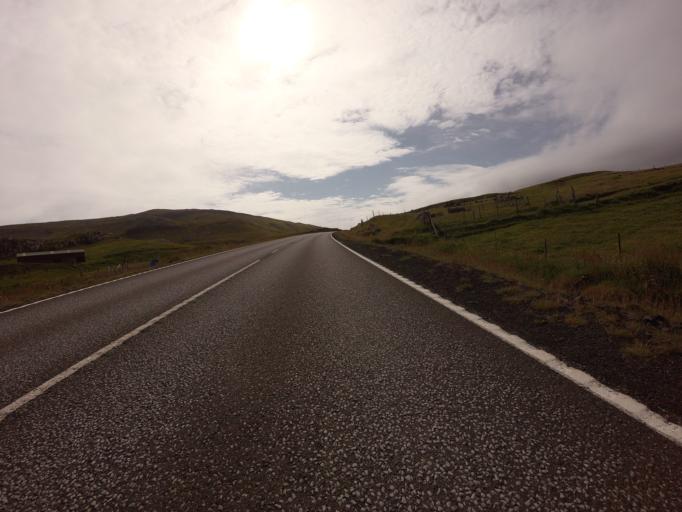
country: FO
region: Sandoy
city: Sandur
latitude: 61.8945
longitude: -6.8660
